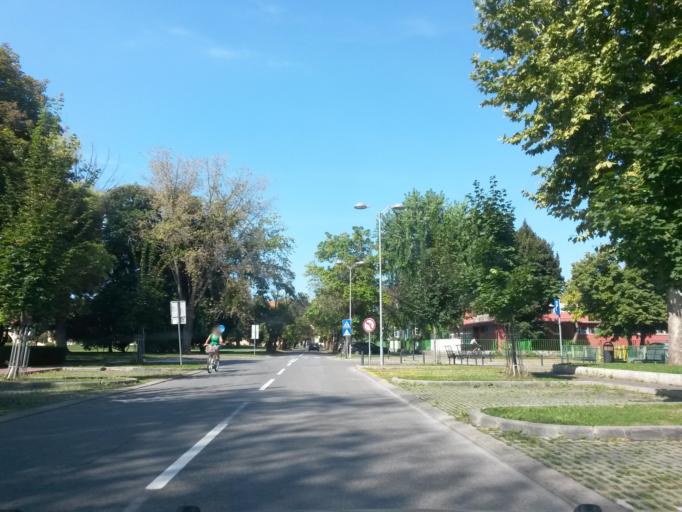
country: HR
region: Osjecko-Baranjska
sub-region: Grad Osijek
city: Osijek
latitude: 45.5573
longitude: 18.6941
